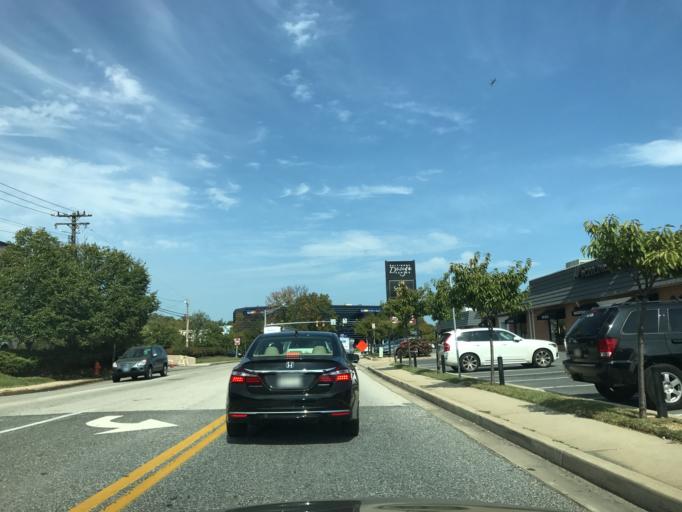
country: US
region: Maryland
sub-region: Baltimore County
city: Timonium
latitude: 39.4395
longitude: -76.6317
